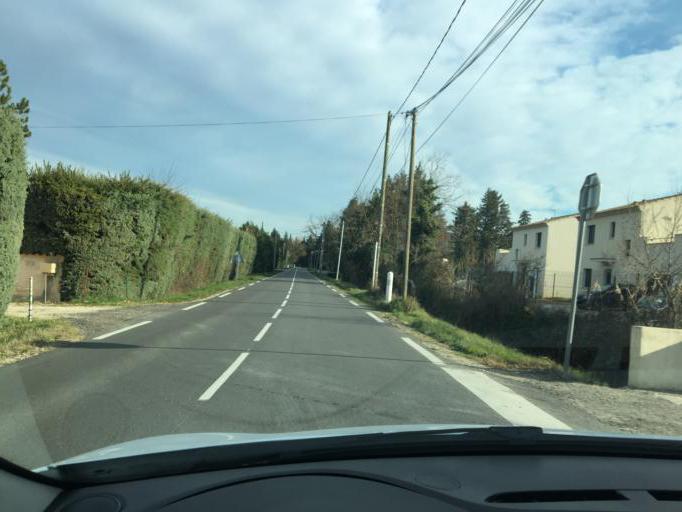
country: FR
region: Provence-Alpes-Cote d'Azur
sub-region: Departement du Vaucluse
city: Caumont-sur-Durance
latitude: 43.9020
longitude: 4.9570
